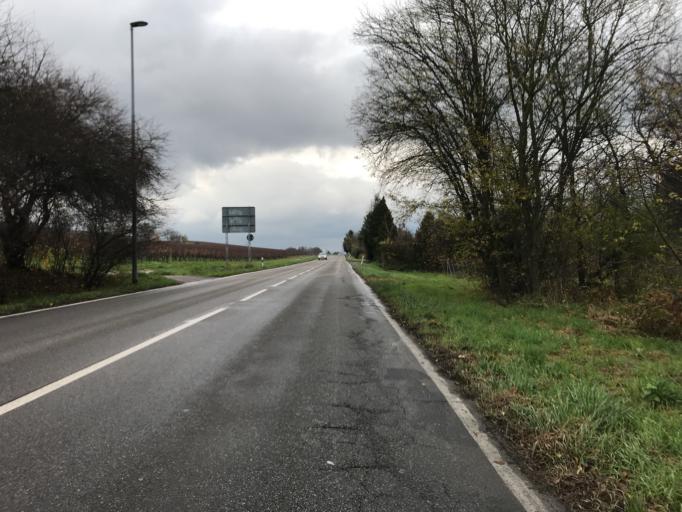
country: DE
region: Rheinland-Pfalz
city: Bodenheim
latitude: 49.9372
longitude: 8.3058
